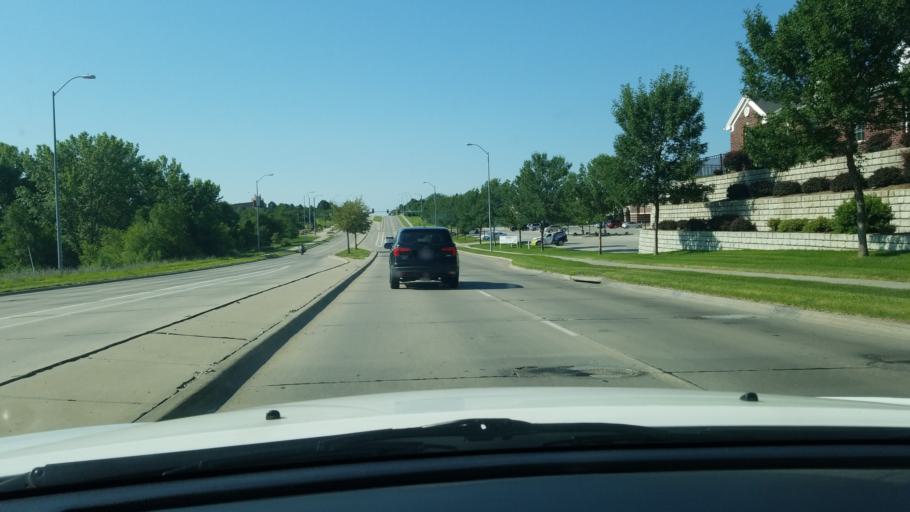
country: US
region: Nebraska
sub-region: Lancaster County
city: Lincoln
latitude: 40.7836
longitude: -96.6061
